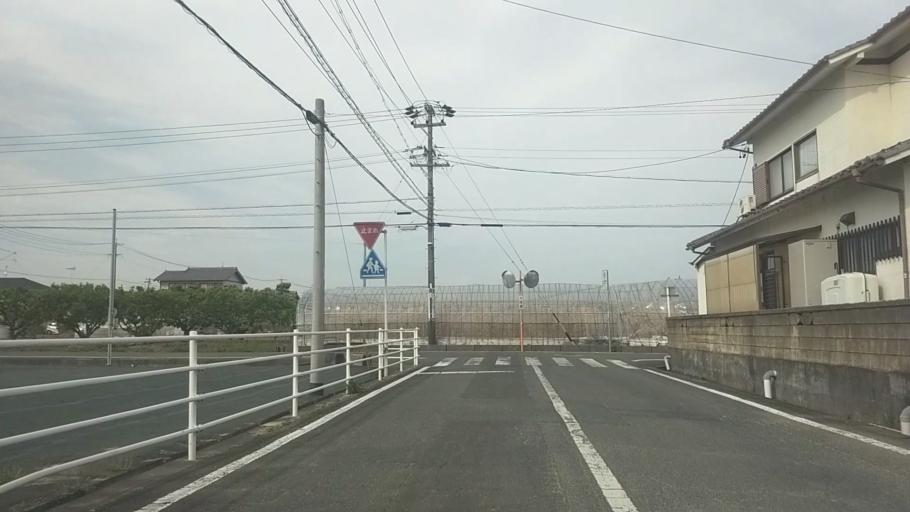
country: JP
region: Shizuoka
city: Hamamatsu
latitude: 34.7213
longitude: 137.6531
